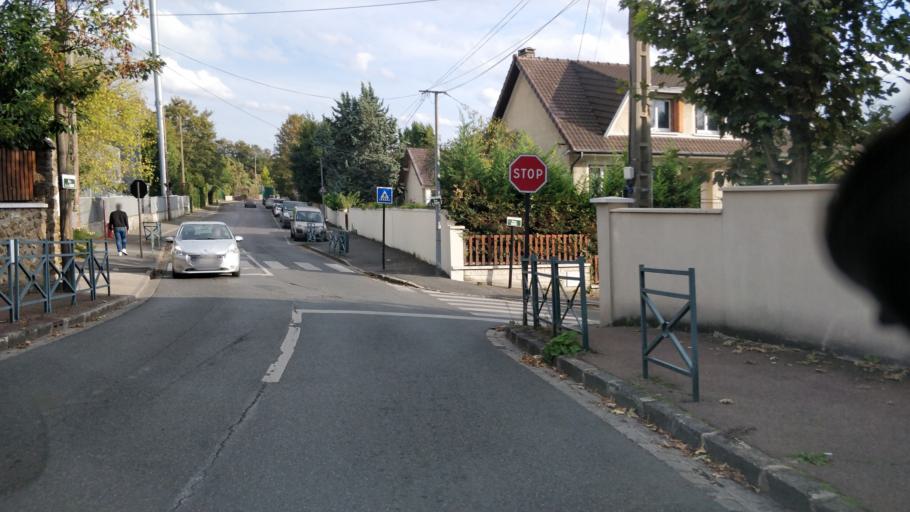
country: FR
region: Ile-de-France
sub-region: Departement de Seine-Saint-Denis
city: Le Raincy
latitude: 48.8915
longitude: 2.5210
